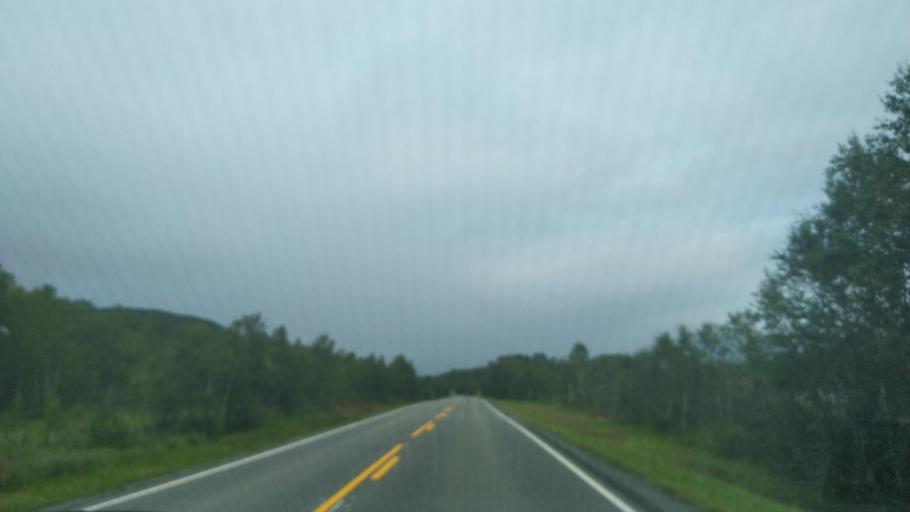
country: NO
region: Nordland
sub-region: Ballangen
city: Ballangen
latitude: 68.4991
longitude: 16.8339
